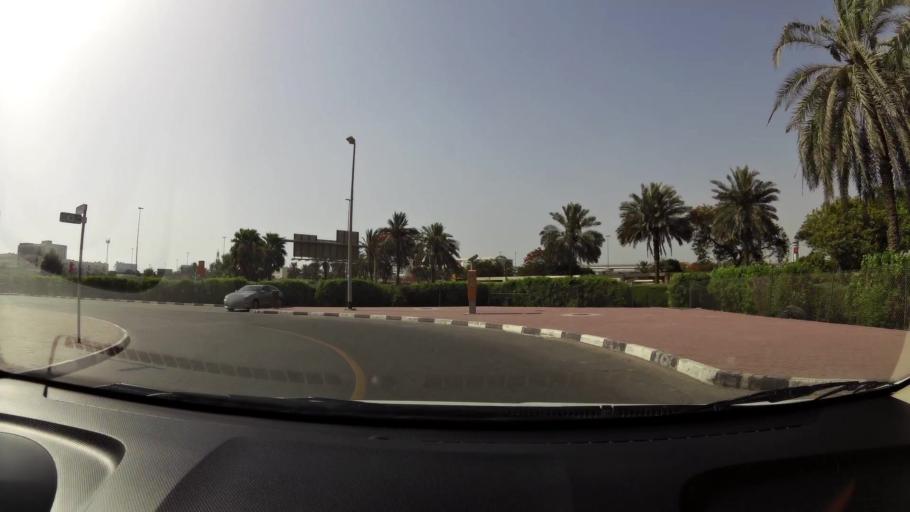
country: AE
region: Ash Shariqah
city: Sharjah
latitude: 25.2450
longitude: 55.3530
